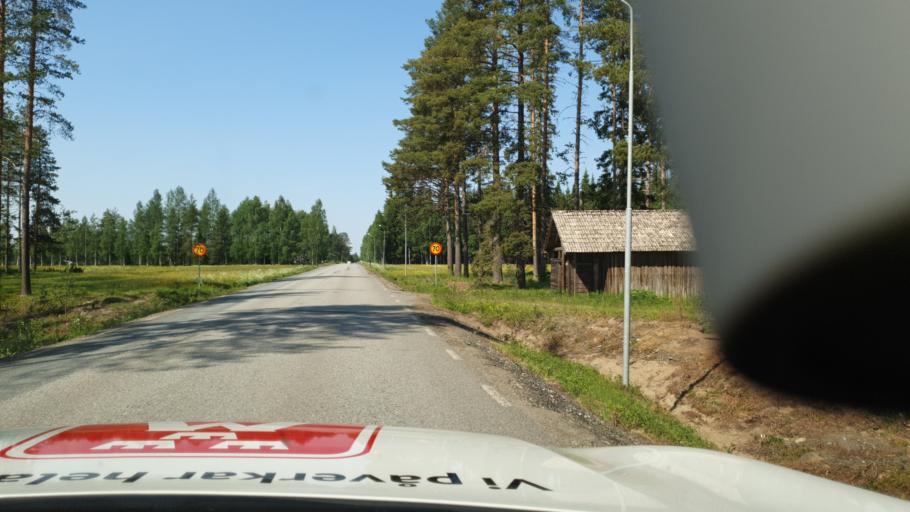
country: SE
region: Vaesterbotten
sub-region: Skelleftea Kommun
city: Langsele
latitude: 64.9404
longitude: 19.9837
